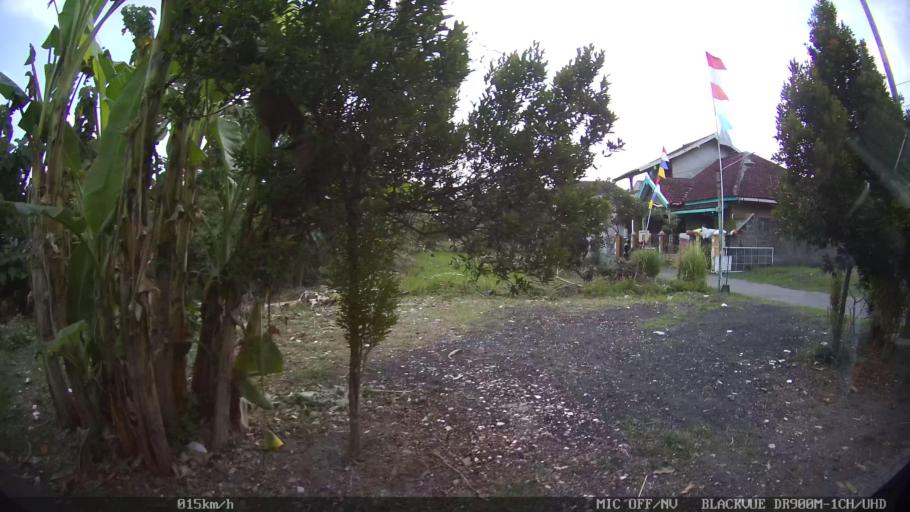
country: ID
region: Daerah Istimewa Yogyakarta
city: Yogyakarta
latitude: -7.8166
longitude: 110.4060
